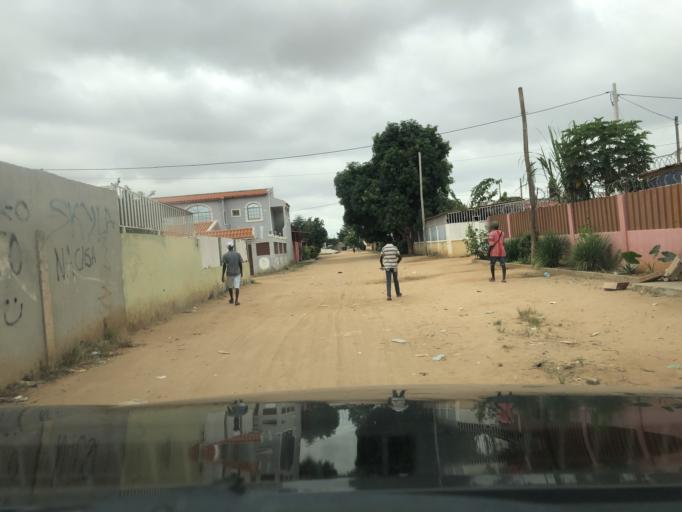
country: AO
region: Luanda
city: Luanda
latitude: -8.9359
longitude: 13.2536
